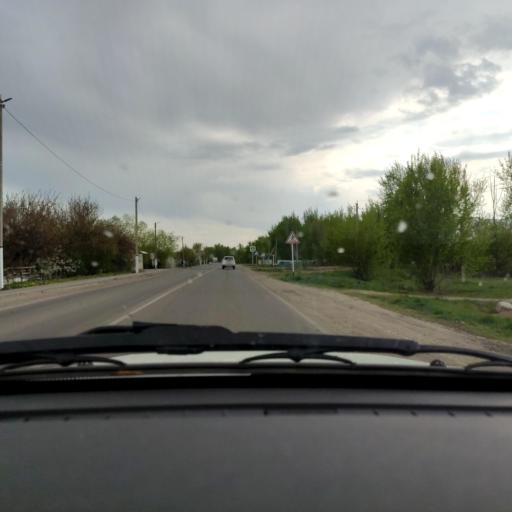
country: RU
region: Voronezj
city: Novaya Usman'
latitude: 51.6096
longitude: 39.3740
